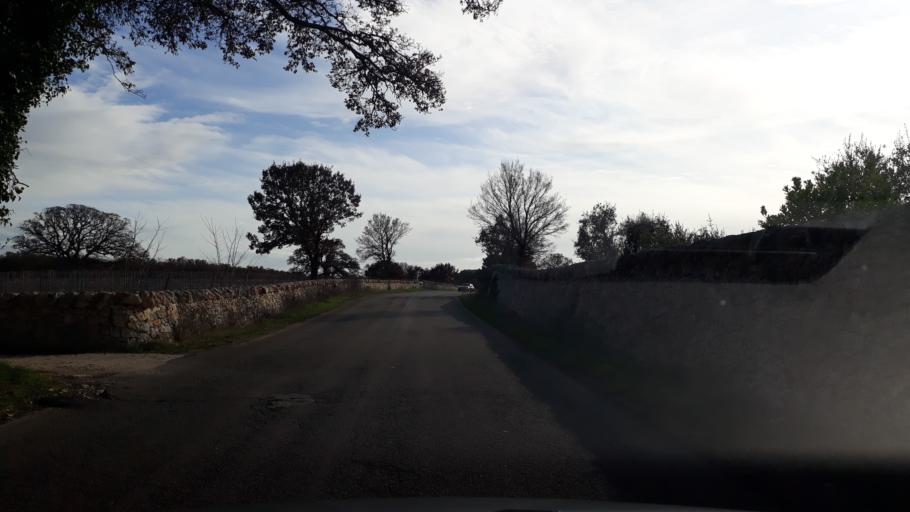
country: IT
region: Apulia
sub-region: Provincia di Taranto
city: Martina Franca
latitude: 40.6760
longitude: 17.3612
